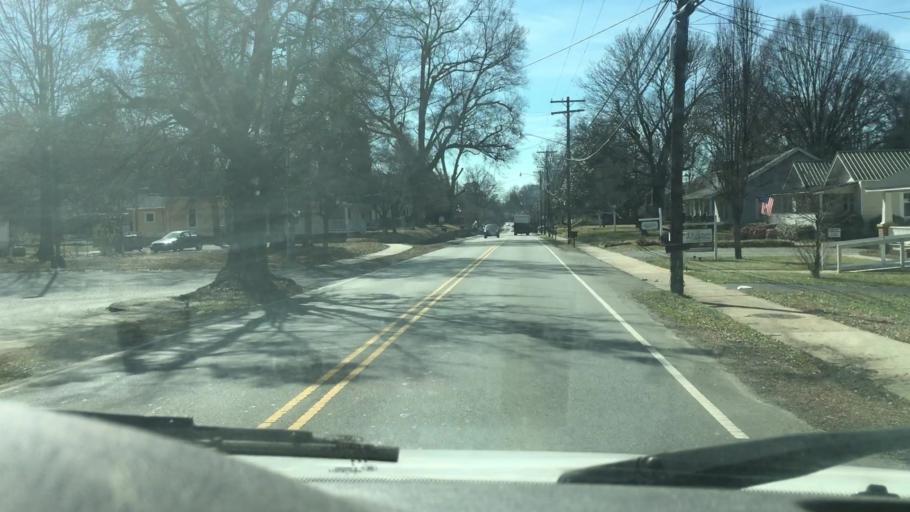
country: US
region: North Carolina
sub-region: Mecklenburg County
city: Cornelius
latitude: 35.4896
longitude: -80.8580
